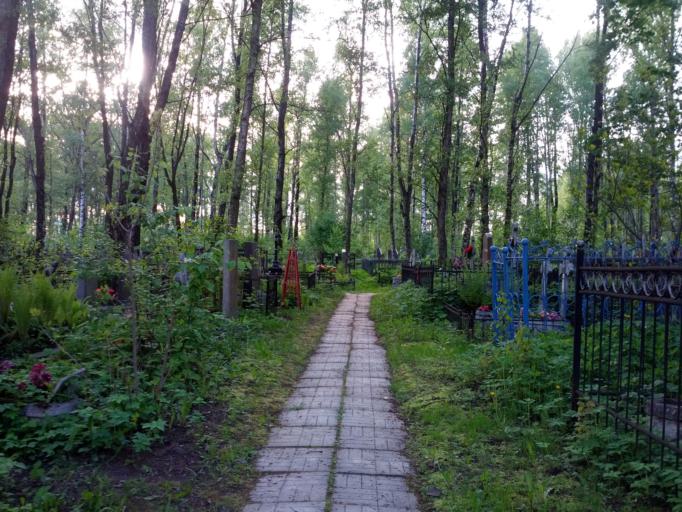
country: RU
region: St.-Petersburg
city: Obukhovo
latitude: 59.9112
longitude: 30.4298
